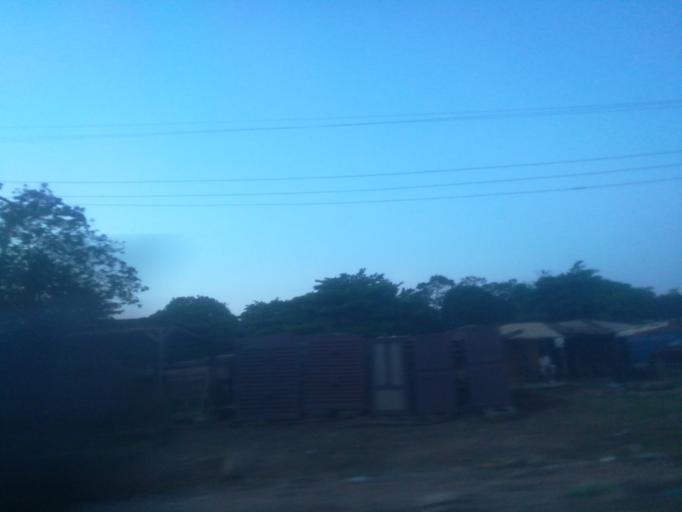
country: NG
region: Ogun
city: Abeokuta
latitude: 7.1864
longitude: 3.4330
